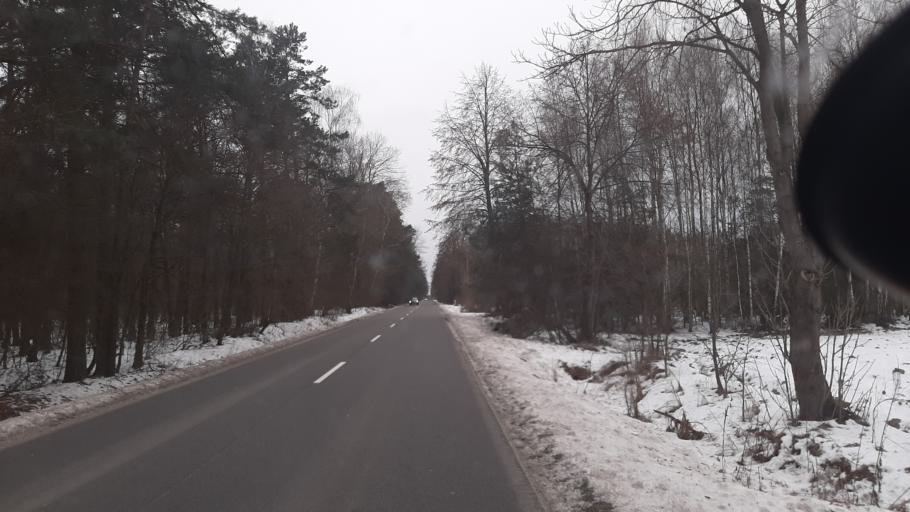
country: PL
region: Lublin Voivodeship
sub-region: Powiat lubartowski
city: Kamionka
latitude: 51.4973
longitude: 22.4138
